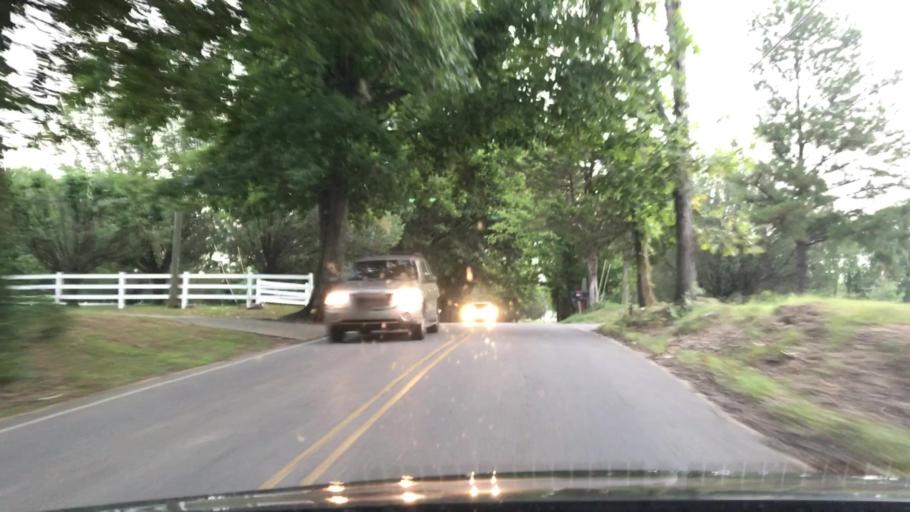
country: US
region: Tennessee
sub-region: Williamson County
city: Nolensville
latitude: 35.9766
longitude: -86.6578
